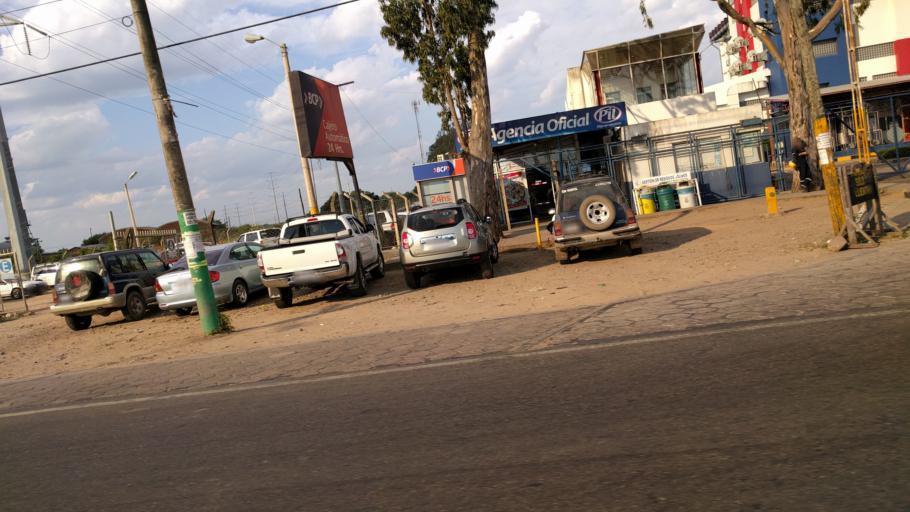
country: BO
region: Santa Cruz
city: Warnes
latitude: -17.5305
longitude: -63.1614
